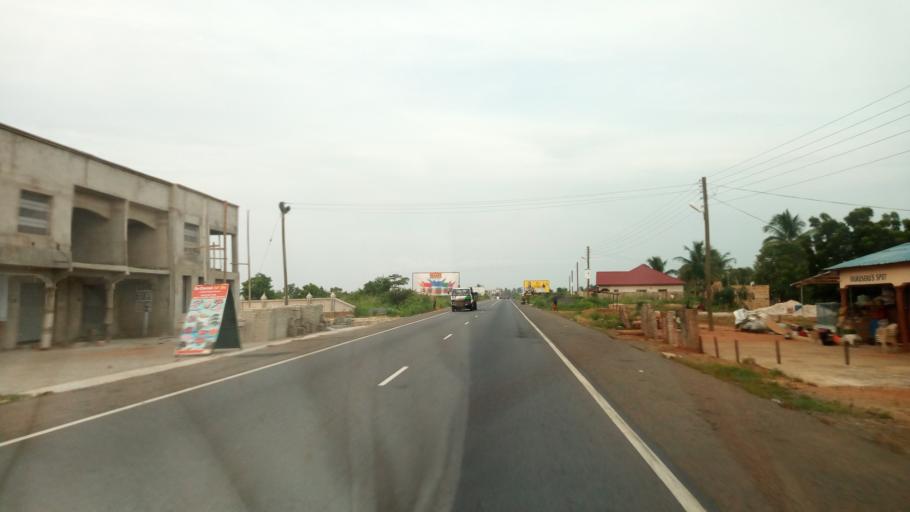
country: TG
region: Maritime
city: Lome
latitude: 6.1116
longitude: 1.1214
